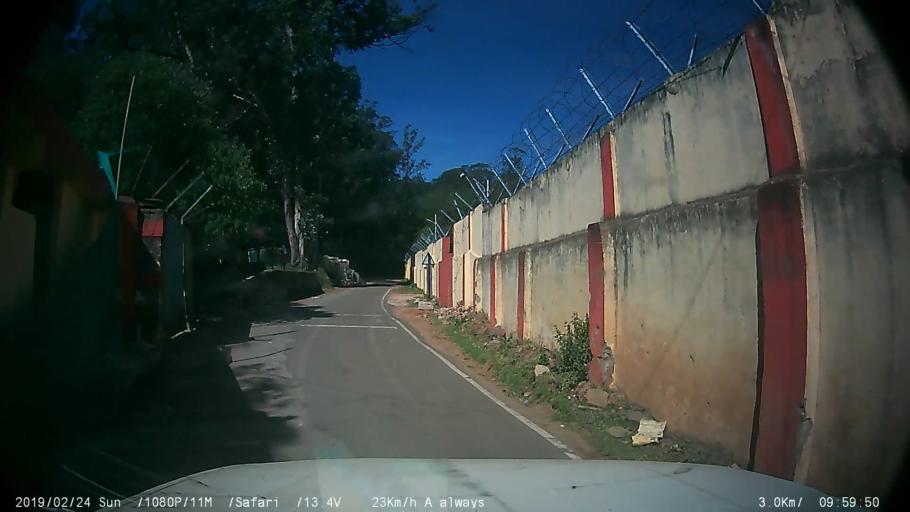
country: IN
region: Tamil Nadu
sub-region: Nilgiri
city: Aravankadu
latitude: 11.3624
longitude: 76.7657
